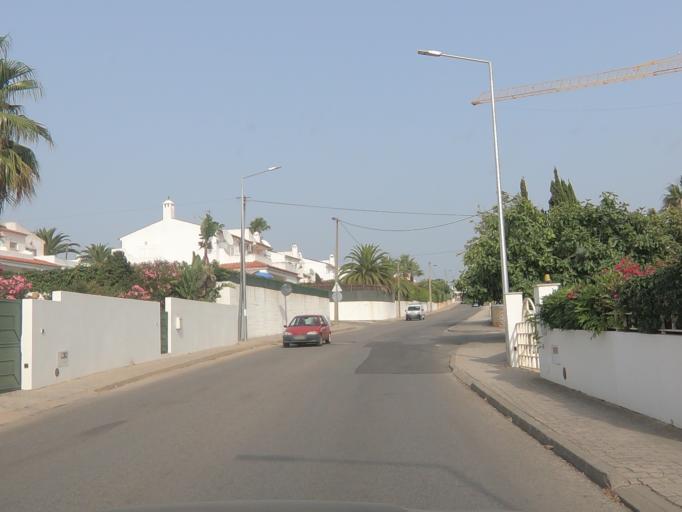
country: PT
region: Faro
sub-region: Albufeira
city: Guia
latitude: 37.0800
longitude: -8.3023
